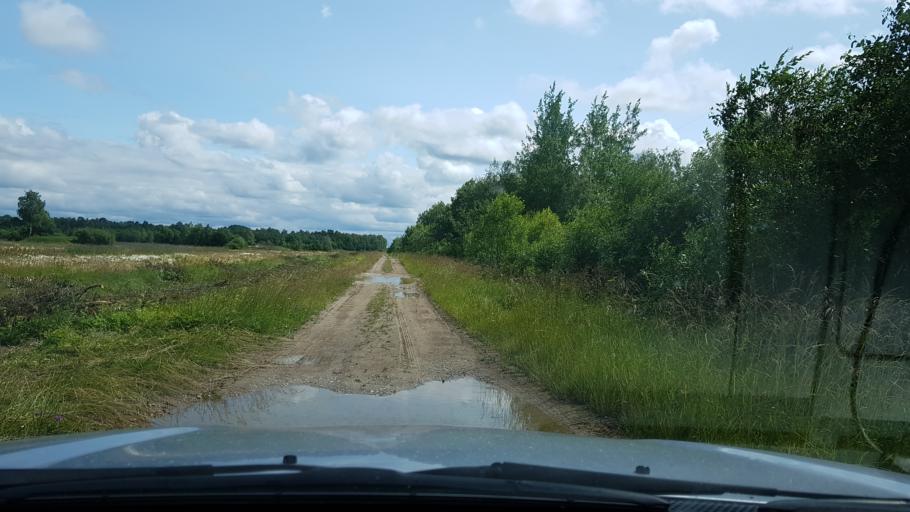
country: EE
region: Ida-Virumaa
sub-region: Sillamaee linn
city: Sillamae
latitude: 59.3615
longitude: 27.8010
